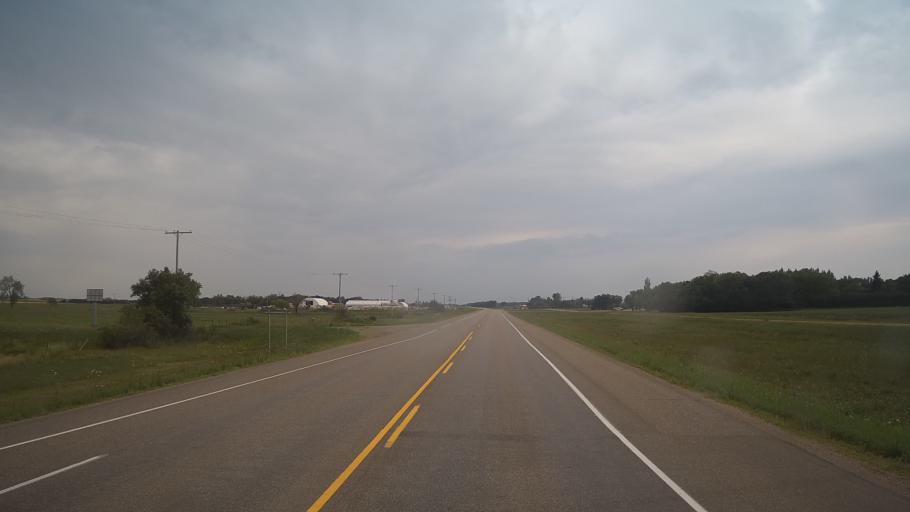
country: CA
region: Saskatchewan
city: Langham
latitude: 52.1289
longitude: -107.2197
